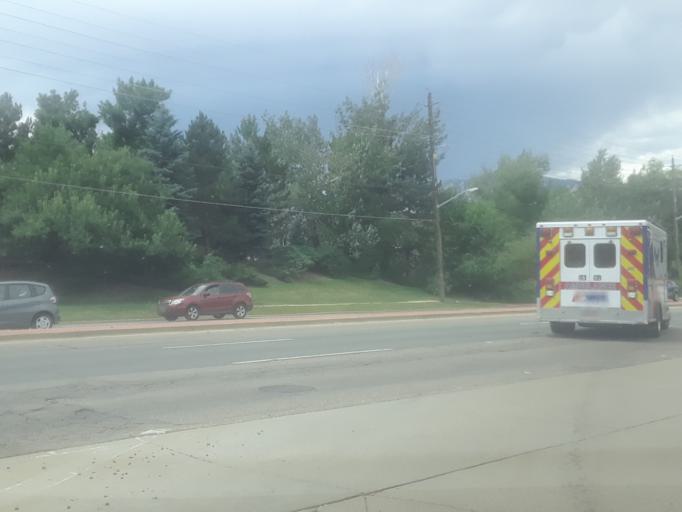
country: US
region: Colorado
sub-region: Boulder County
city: Boulder
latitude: 40.0149
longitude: -105.2350
